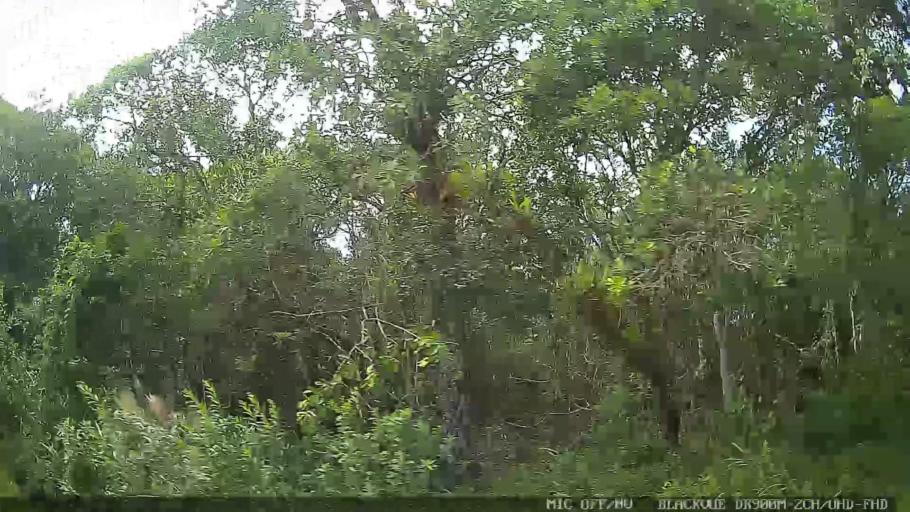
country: BR
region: Sao Paulo
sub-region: Iguape
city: Iguape
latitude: -24.7194
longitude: -47.5238
